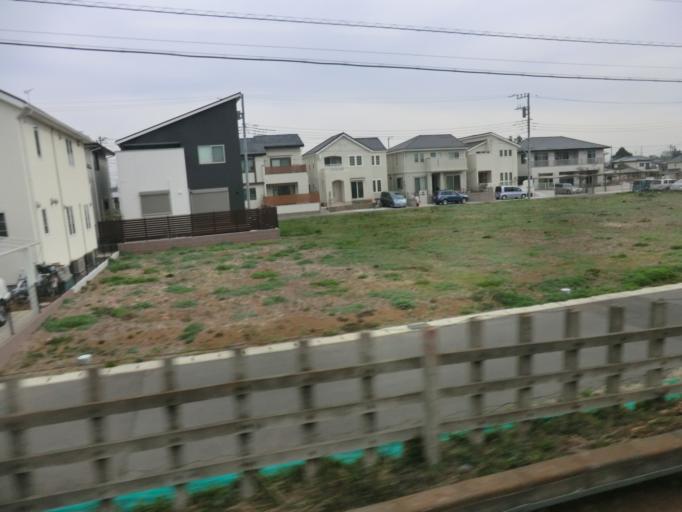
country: JP
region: Chiba
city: Nagareyama
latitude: 35.8702
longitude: 139.9305
